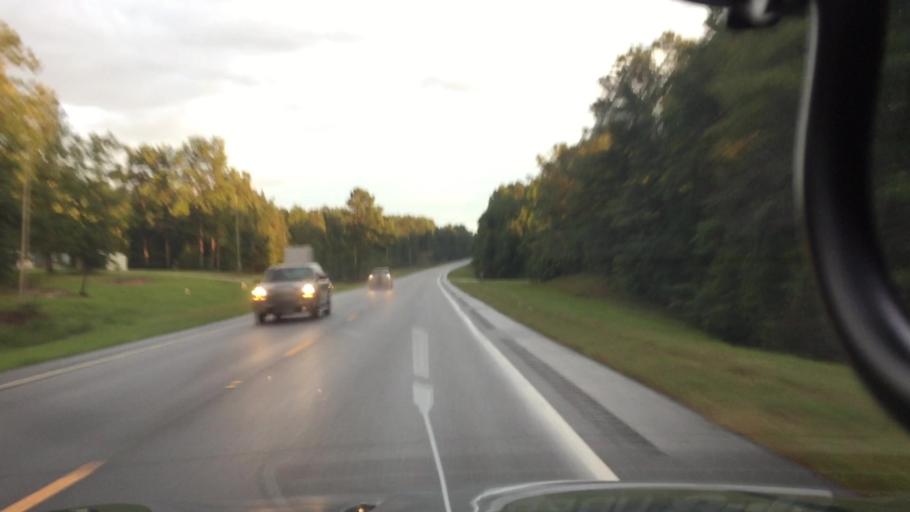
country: US
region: Alabama
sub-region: Coffee County
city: New Brockton
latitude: 31.5555
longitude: -85.9216
